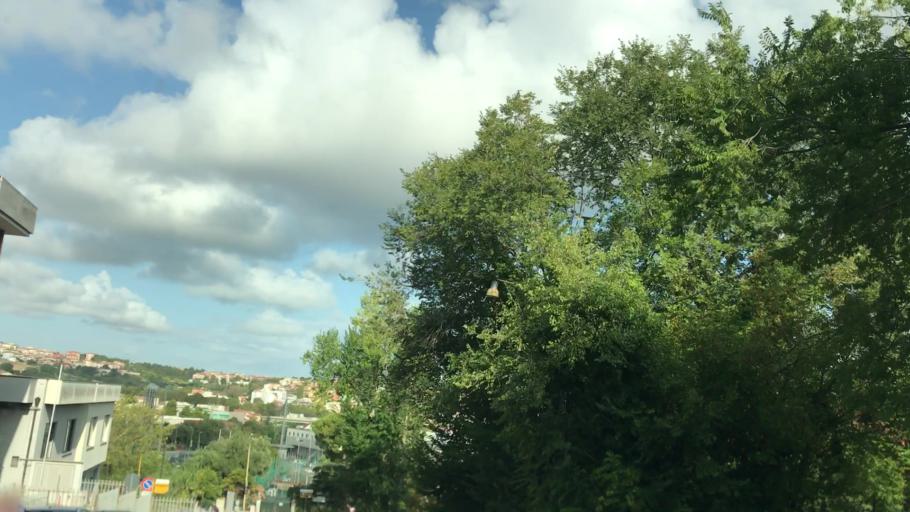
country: IT
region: The Marches
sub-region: Provincia di Ancona
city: Le Grazie di Ancona
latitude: 43.5951
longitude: 13.5139
